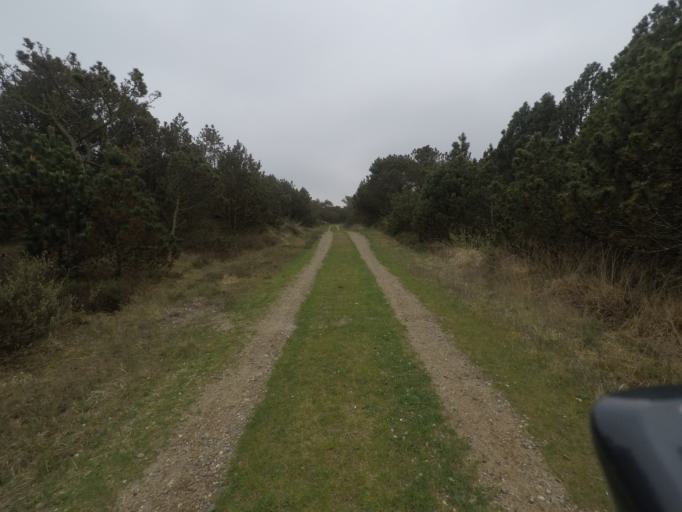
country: DE
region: Schleswig-Holstein
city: List
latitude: 55.1231
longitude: 8.5224
